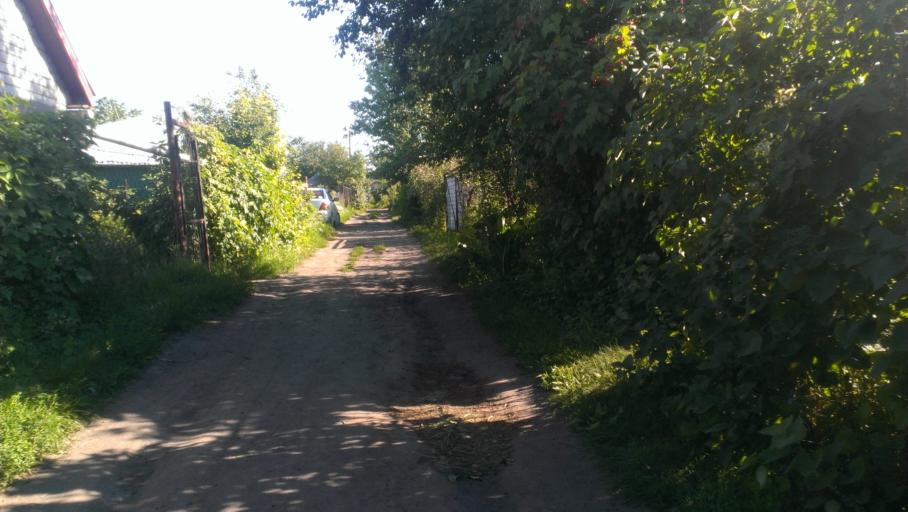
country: RU
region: Altai Krai
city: Novosilikatnyy
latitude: 53.3228
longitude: 83.6695
